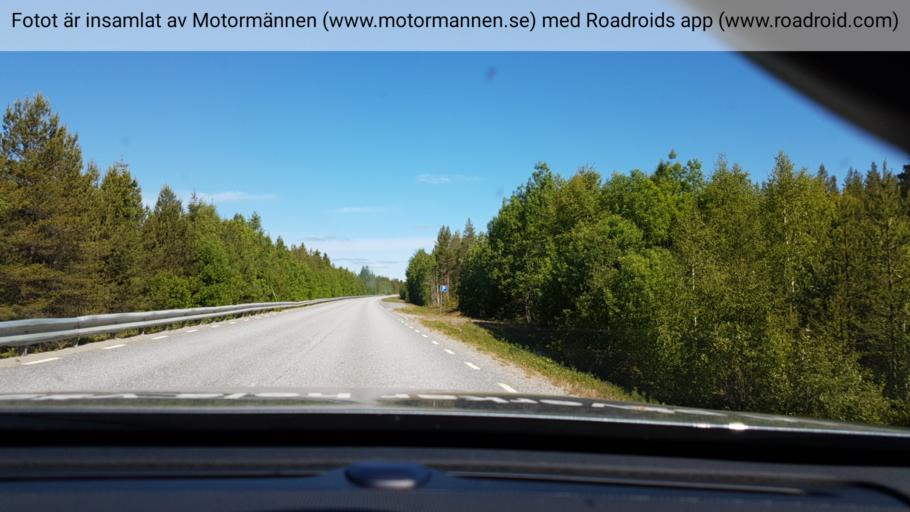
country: SE
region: Vaesterbotten
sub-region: Vilhelmina Kommun
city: Vilhelmina
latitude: 64.4276
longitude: 16.8044
